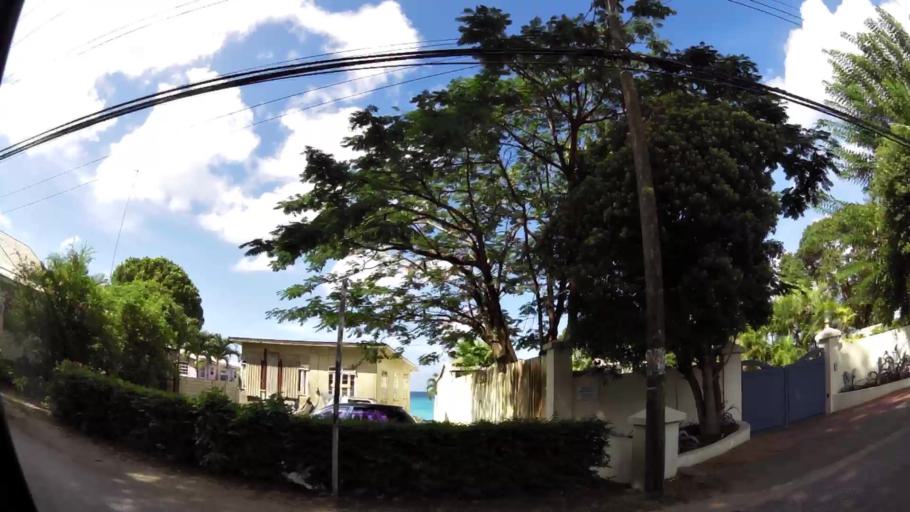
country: BB
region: Saint James
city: Holetown
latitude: 13.2083
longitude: -59.6395
